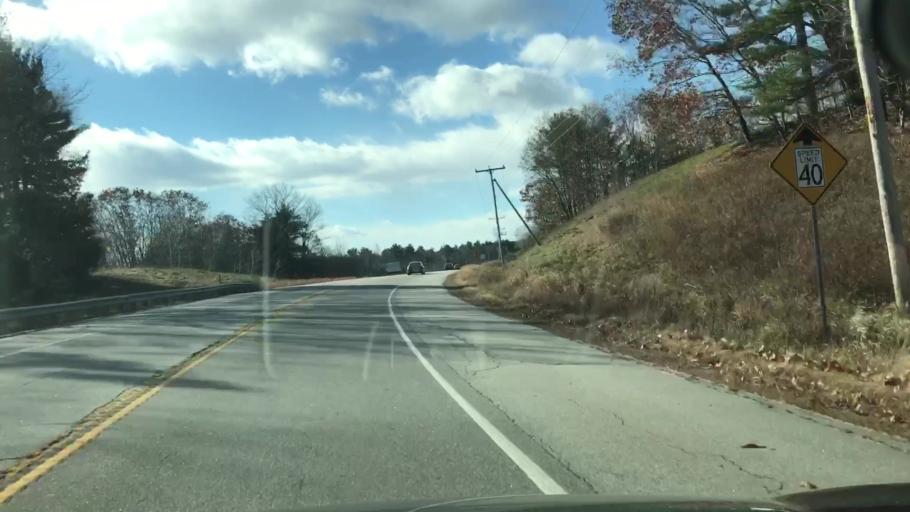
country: US
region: New Hampshire
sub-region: Merrimack County
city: Pittsfield
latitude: 43.3169
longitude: -71.3078
